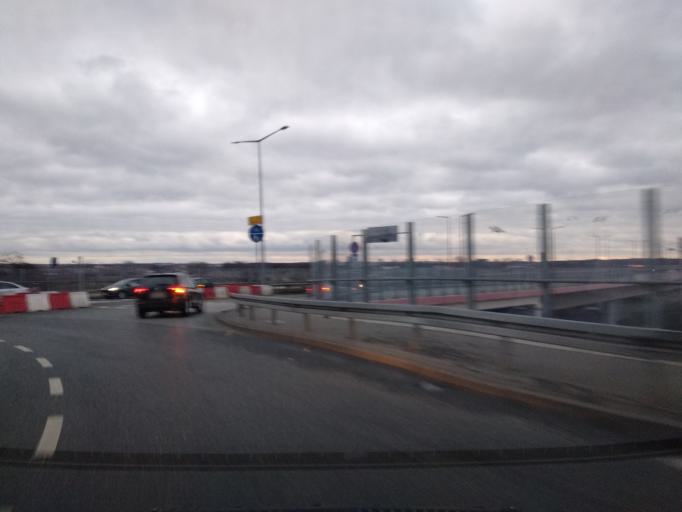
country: PL
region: Greater Poland Voivodeship
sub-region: Konin
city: Konin
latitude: 52.2262
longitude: 18.2438
